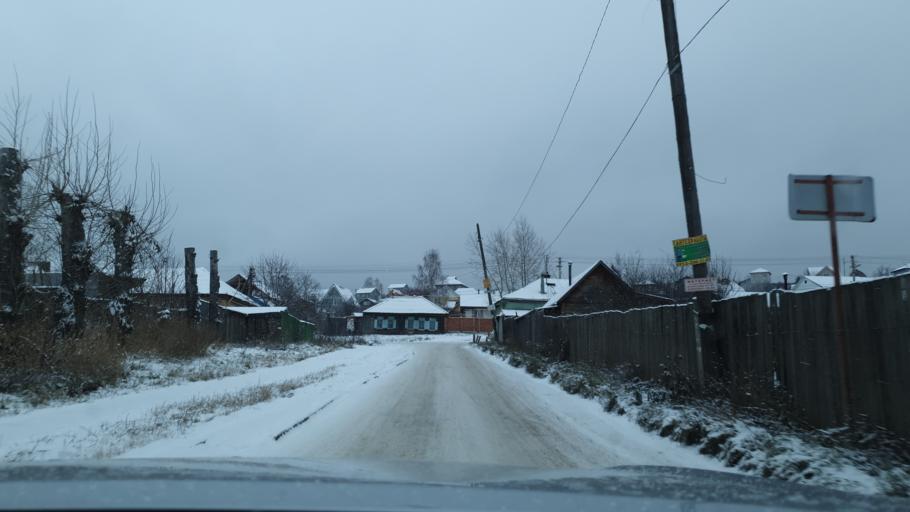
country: RU
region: Sverdlovsk
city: Istok
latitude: 56.7482
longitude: 60.6997
